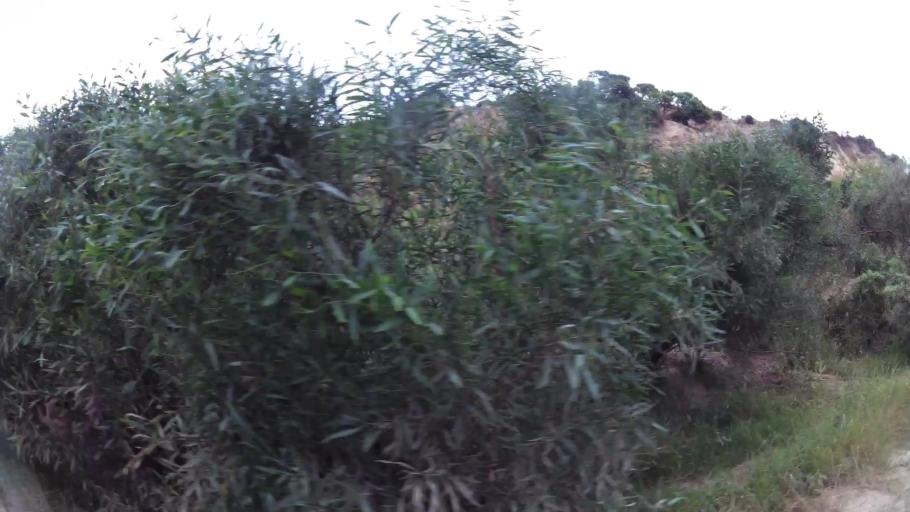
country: MA
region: Rabat-Sale-Zemmour-Zaer
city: Sale
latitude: 34.0059
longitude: -6.7808
